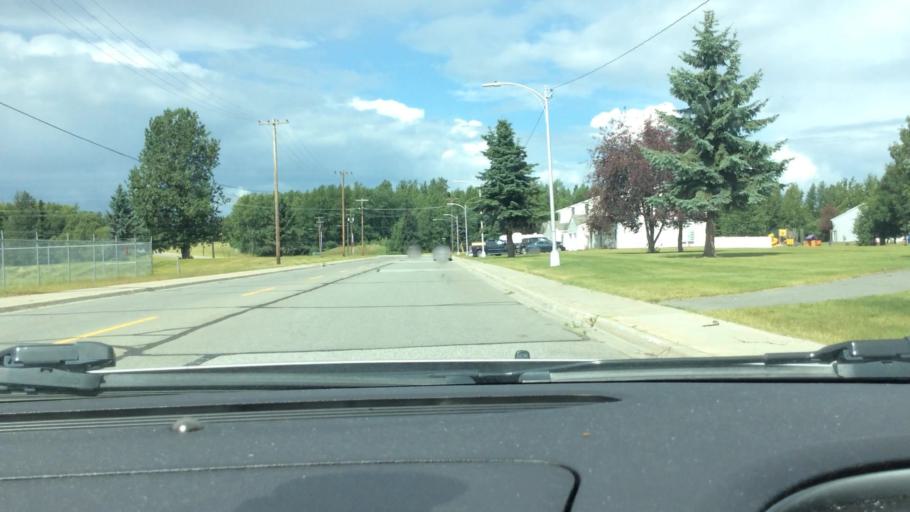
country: US
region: Alaska
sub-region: Anchorage Municipality
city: Anchorage
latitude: 61.2346
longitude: -149.8682
